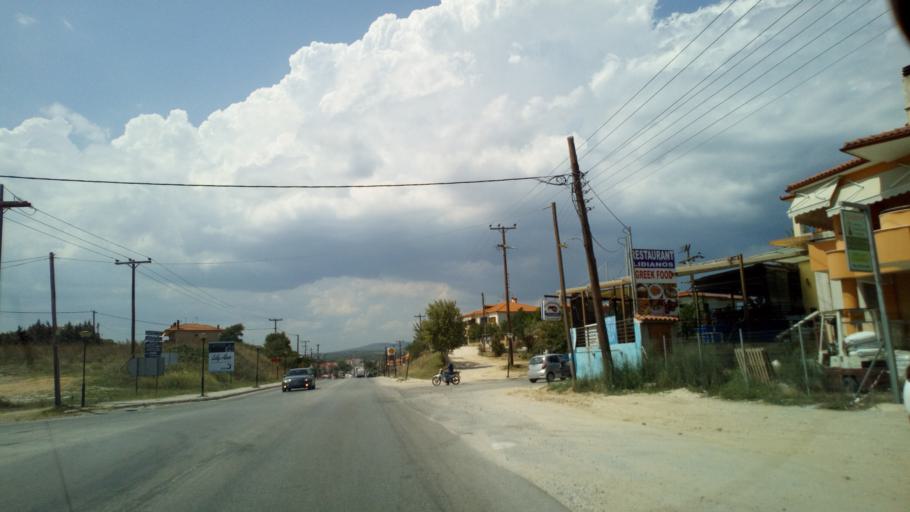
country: GR
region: Central Macedonia
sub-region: Nomos Chalkidikis
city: Nikiti
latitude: 40.2203
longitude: 23.6723
